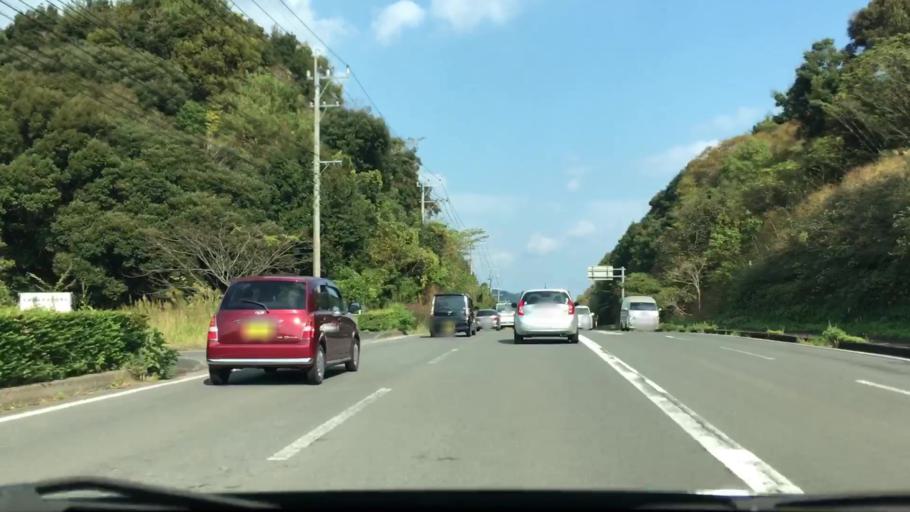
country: JP
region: Nagasaki
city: Sasebo
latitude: 32.9912
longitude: 129.7496
